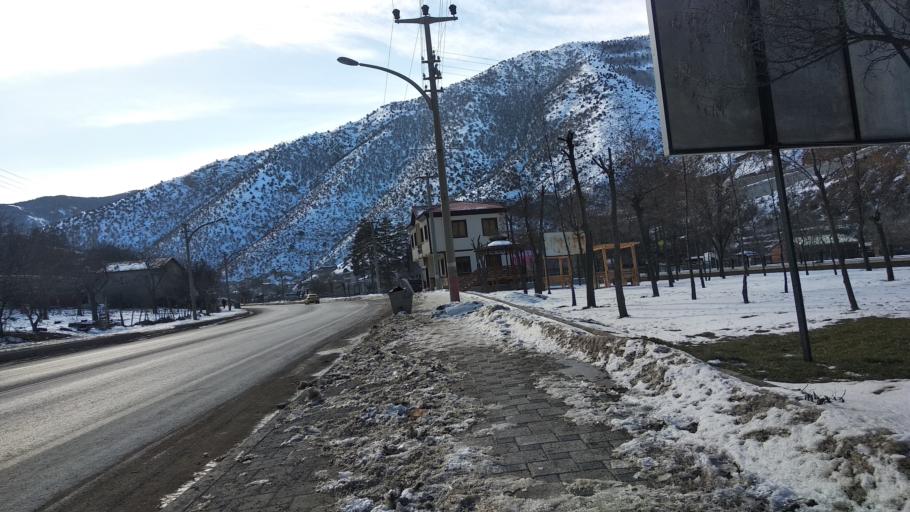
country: TR
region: Gumushane
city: Gumushkhane
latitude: 40.4441
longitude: 39.5036
